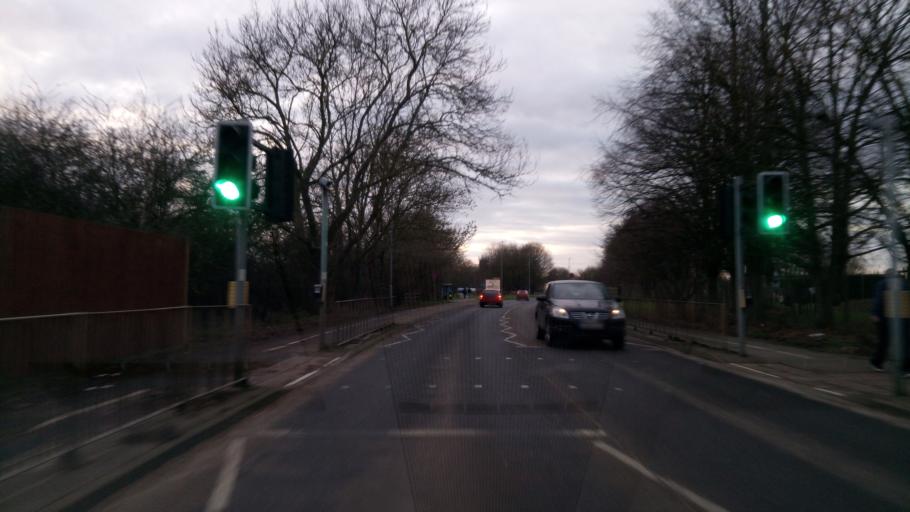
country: GB
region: England
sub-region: Peterborough
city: Peterborough
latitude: 52.5512
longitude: -0.2229
